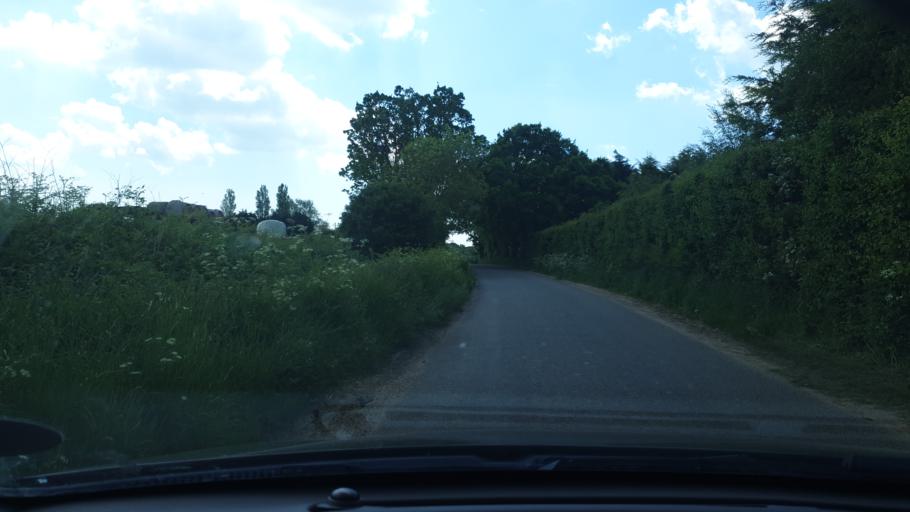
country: GB
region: England
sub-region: Essex
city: Great Bentley
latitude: 51.8447
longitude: 1.0903
